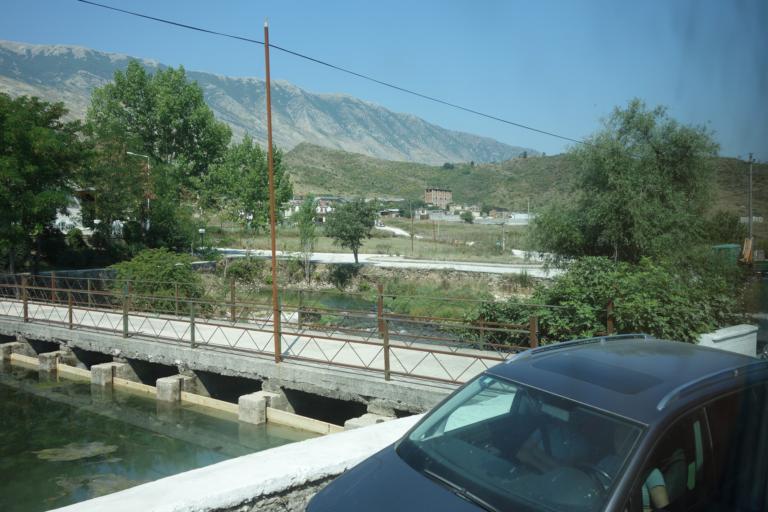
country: AL
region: Gjirokaster
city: Gjirokaster
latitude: 40.1031
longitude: 20.1241
